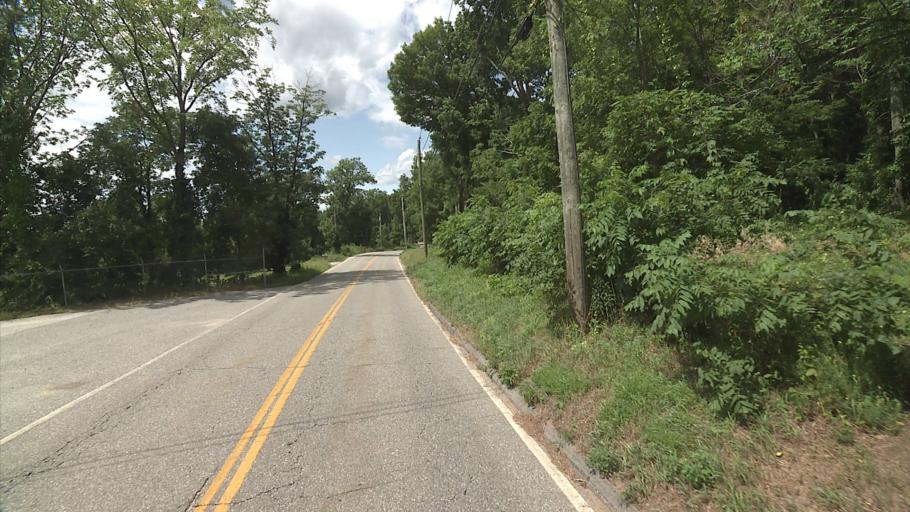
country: US
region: Connecticut
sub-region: Windham County
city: South Windham
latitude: 41.6412
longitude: -72.1840
